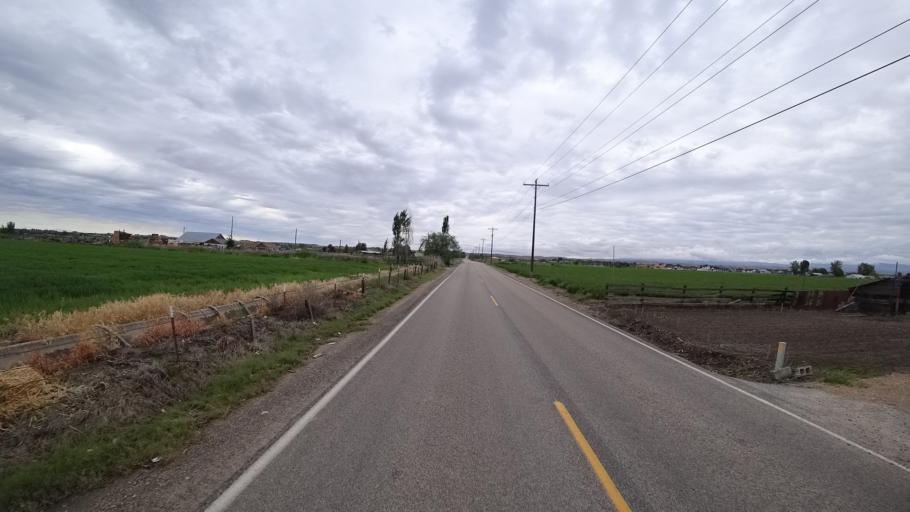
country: US
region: Idaho
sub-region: Ada County
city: Star
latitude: 43.6949
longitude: -116.4435
